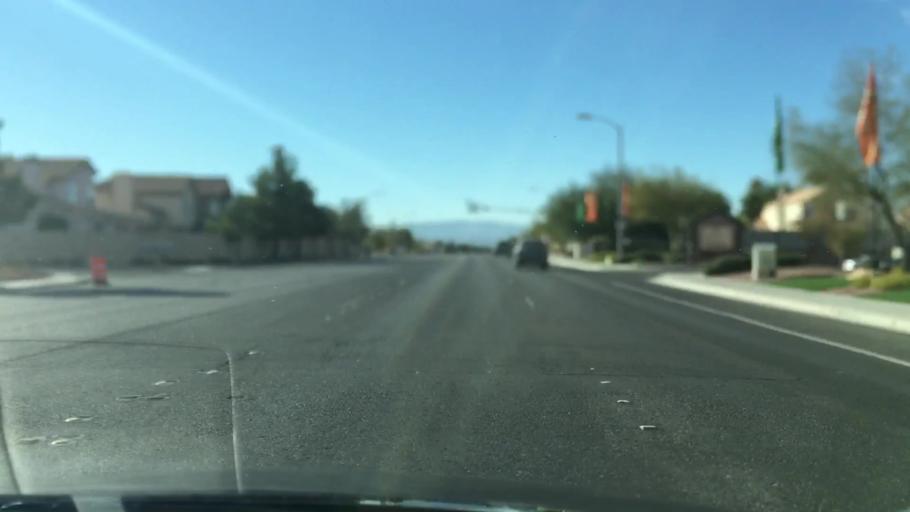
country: US
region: Nevada
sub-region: Clark County
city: Whitney
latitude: 36.0498
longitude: -115.1017
